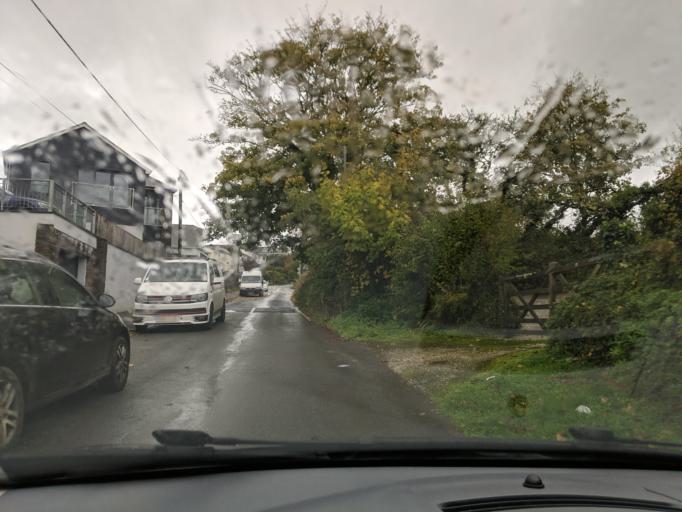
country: GB
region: England
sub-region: Cornwall
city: Wadebridge
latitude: 50.5151
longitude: -4.8213
